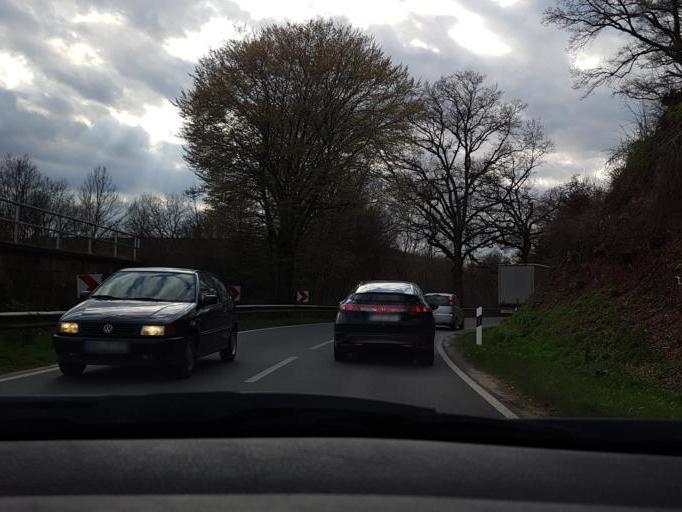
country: DE
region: Lower Saxony
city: Bodenfelde
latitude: 51.6263
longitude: 9.5756
